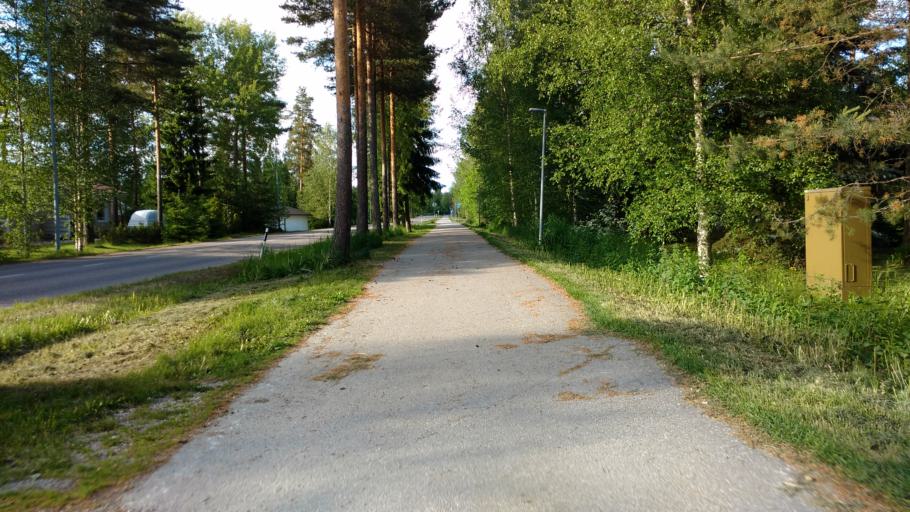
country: FI
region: Varsinais-Suomi
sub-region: Salo
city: Salo
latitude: 60.3912
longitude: 23.1852
